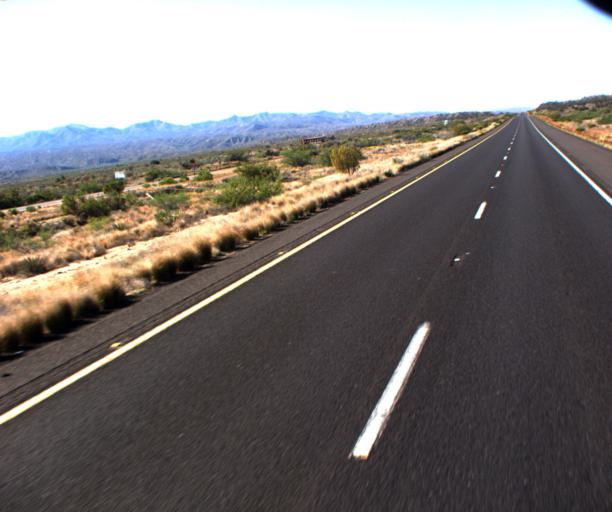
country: US
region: Arizona
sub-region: Mohave County
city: Kingman
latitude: 35.1024
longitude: -113.6665
